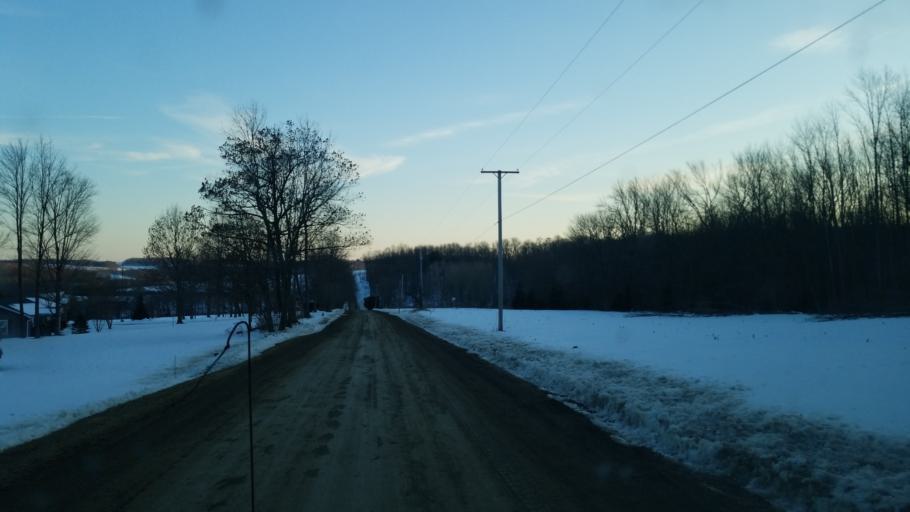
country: US
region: Pennsylvania
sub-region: Tioga County
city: Westfield
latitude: 42.0387
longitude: -77.6197
